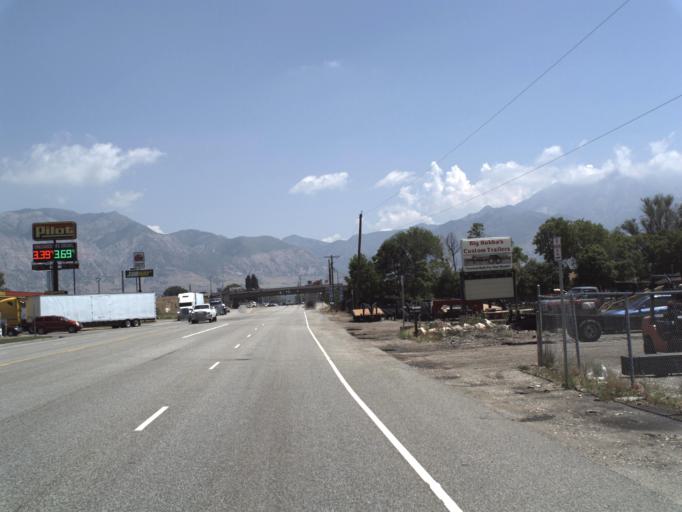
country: US
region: Utah
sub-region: Weber County
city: Marriott-Slaterville
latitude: 41.2448
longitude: -112.0242
